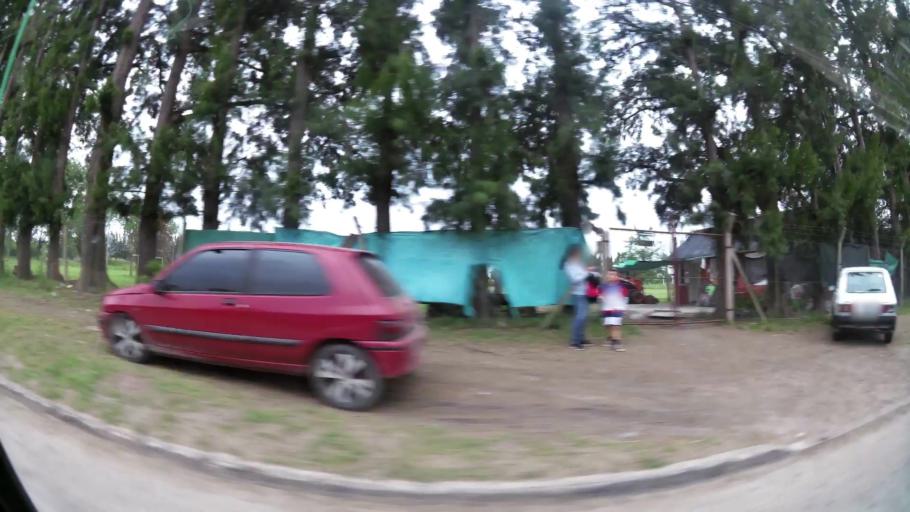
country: AR
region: Buenos Aires
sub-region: Partido de La Plata
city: La Plata
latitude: -34.9374
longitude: -58.0026
